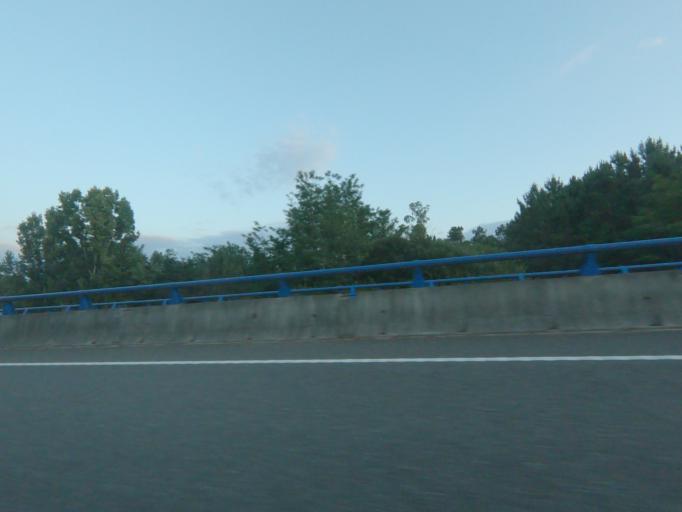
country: ES
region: Galicia
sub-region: Provincia de Pontevedra
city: Ponteareas
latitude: 42.1542
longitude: -8.5149
